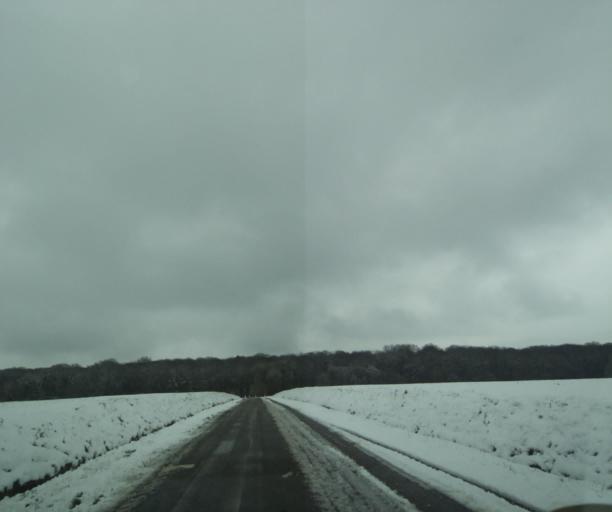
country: FR
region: Champagne-Ardenne
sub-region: Departement de la Haute-Marne
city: Laneuville-a-Remy
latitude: 48.3967
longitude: 4.8643
